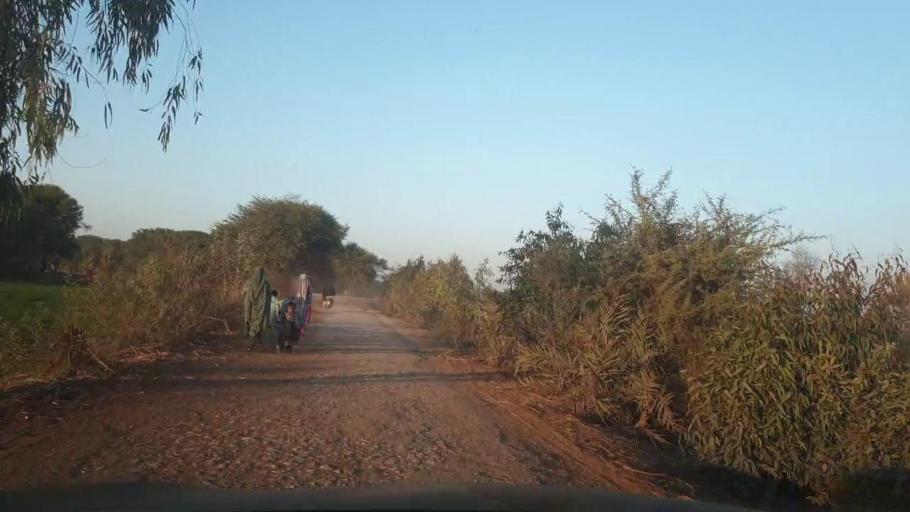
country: PK
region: Sindh
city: Ubauro
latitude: 28.1843
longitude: 69.6021
